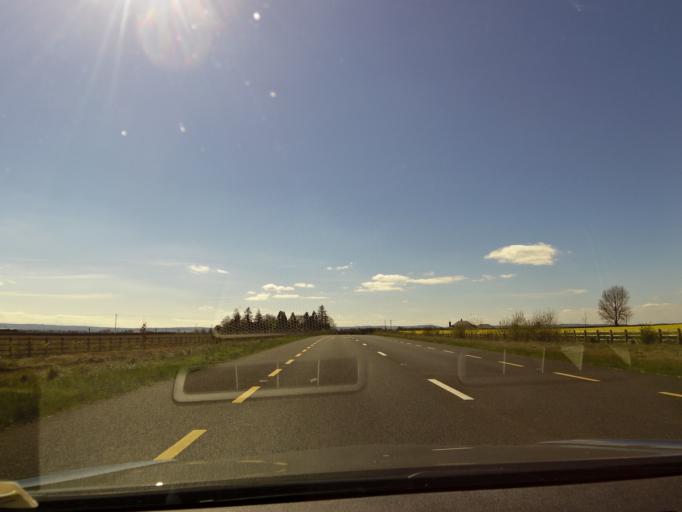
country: IE
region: Leinster
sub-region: Kildare
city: Moone
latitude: 52.9950
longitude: -6.8857
